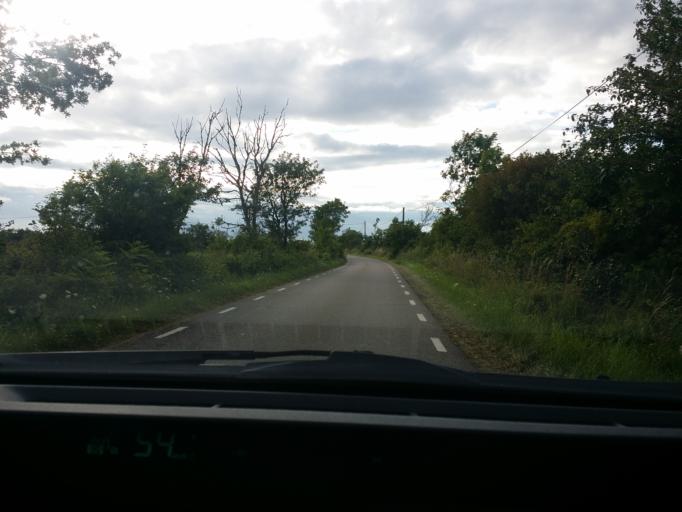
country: SE
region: Kalmar
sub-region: Borgholms Kommun
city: Borgholm
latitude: 57.1154
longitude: 16.9715
